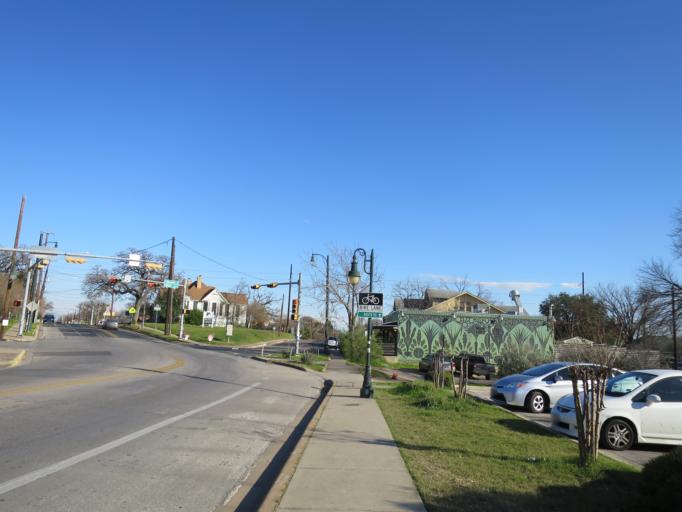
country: US
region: Texas
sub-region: Travis County
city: Austin
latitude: 30.2685
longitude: -97.7274
